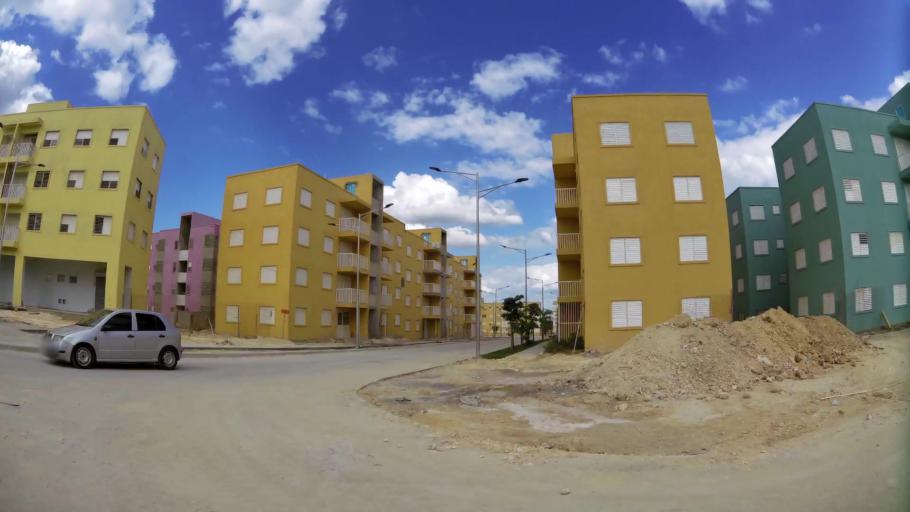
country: DO
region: Nacional
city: Ensanche Luperon
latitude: 18.5277
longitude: -69.8831
